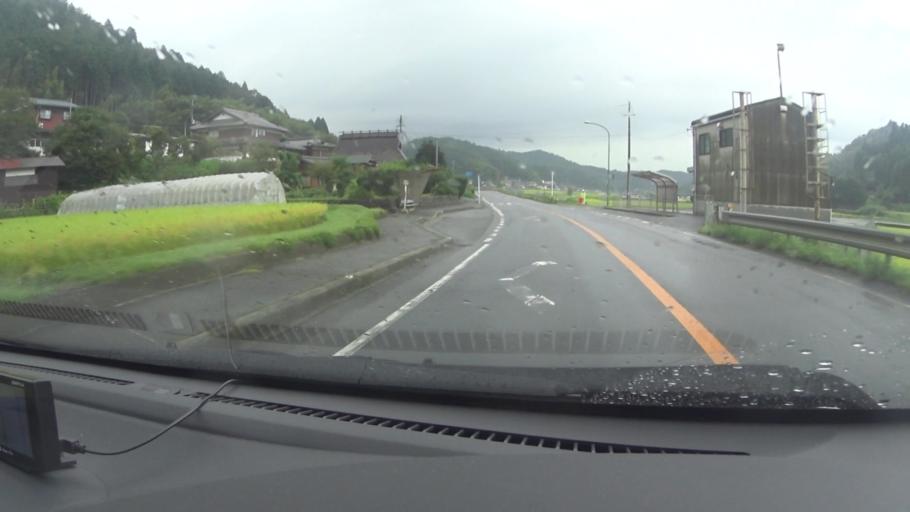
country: JP
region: Kyoto
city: Ayabe
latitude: 35.2048
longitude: 135.3530
